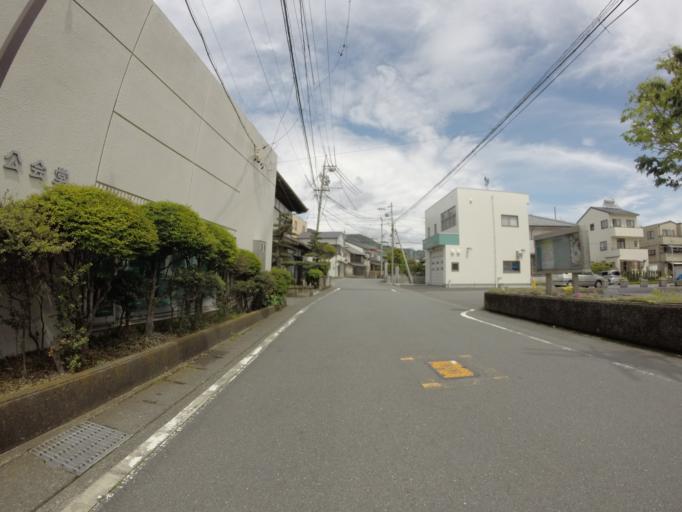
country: JP
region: Shizuoka
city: Fujinomiya
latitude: 35.1061
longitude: 138.5615
